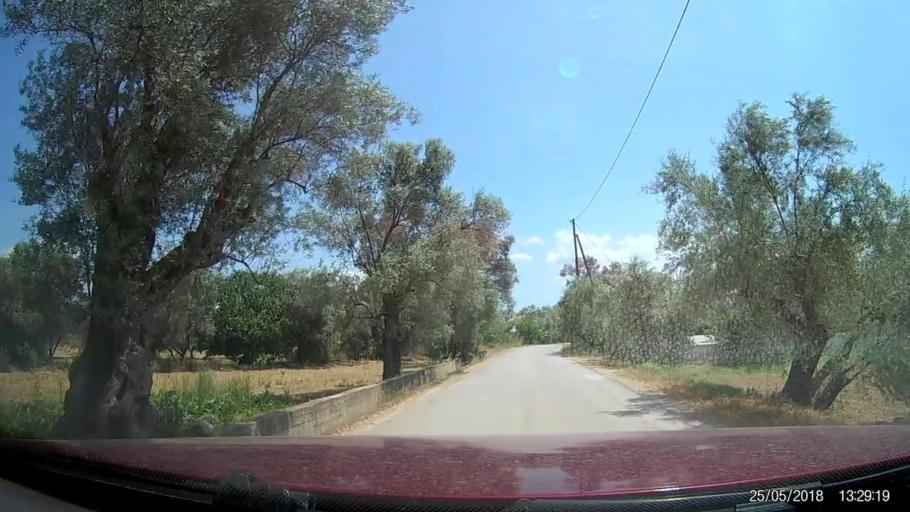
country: GR
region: Central Greece
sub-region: Nomos Evvoias
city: Mytikas
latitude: 38.4436
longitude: 23.6579
